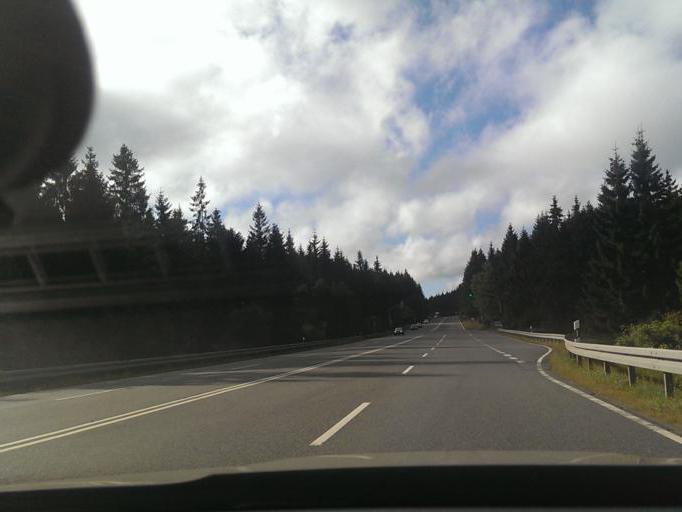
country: DE
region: Lower Saxony
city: Bad Harzburg
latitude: 51.8309
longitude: 10.5234
